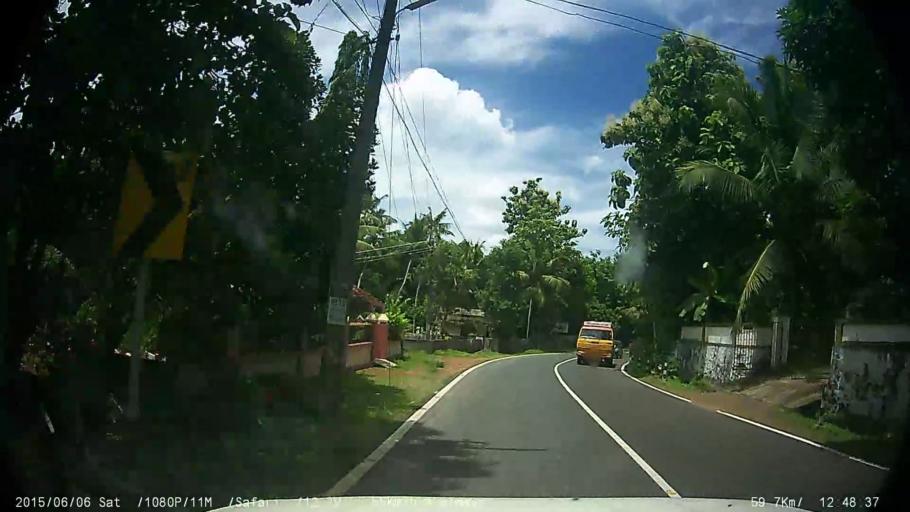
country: IN
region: Kerala
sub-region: Kottayam
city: Kottayam
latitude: 9.5436
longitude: 76.5615
